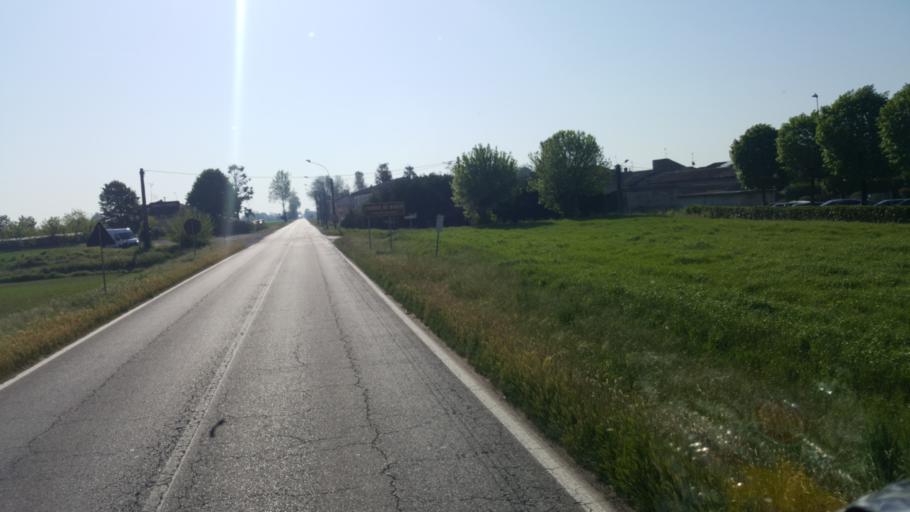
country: IT
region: Lombardy
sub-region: Provincia di Cremona
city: Torre de' Picenardi
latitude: 45.1414
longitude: 10.3169
